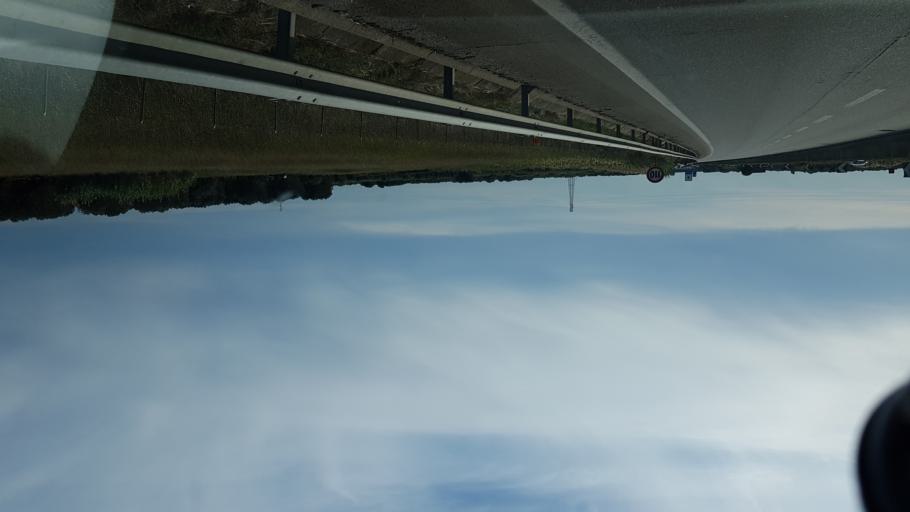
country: IT
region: Apulia
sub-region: Provincia di Brindisi
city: Tuturano
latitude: 40.5503
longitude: 17.9970
